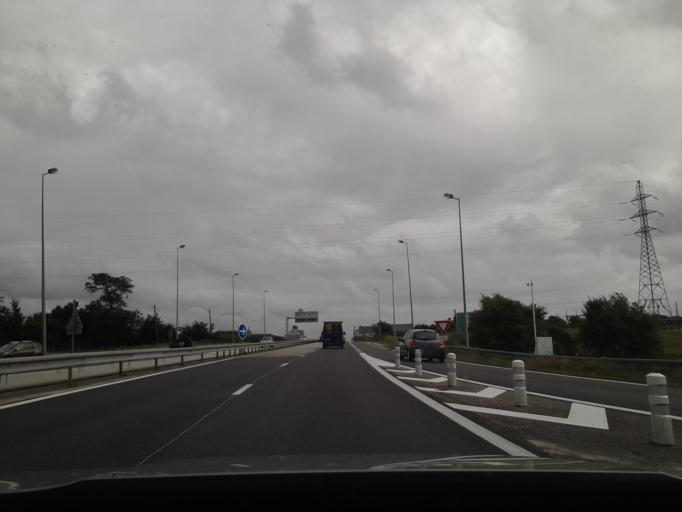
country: FR
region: Lower Normandy
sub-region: Departement de la Manche
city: La Glacerie
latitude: 49.5989
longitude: -1.5972
